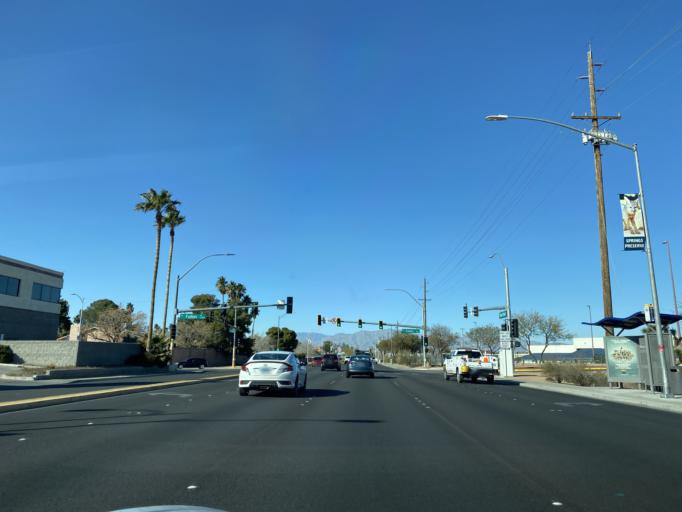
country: US
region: Nevada
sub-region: Clark County
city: Las Vegas
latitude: 36.1622
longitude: -115.1925
